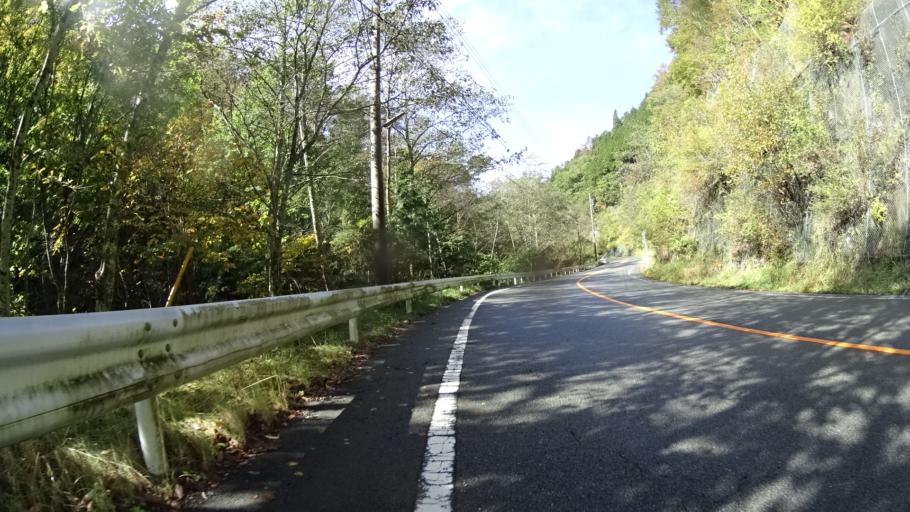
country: JP
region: Yamanashi
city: Enzan
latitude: 35.8063
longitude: 138.8307
